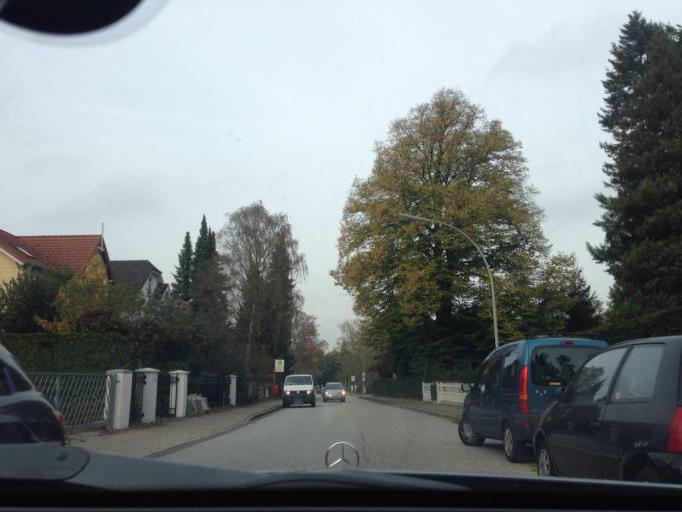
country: DE
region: Schleswig-Holstein
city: Barsbuettel
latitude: 53.5984
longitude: 10.1630
